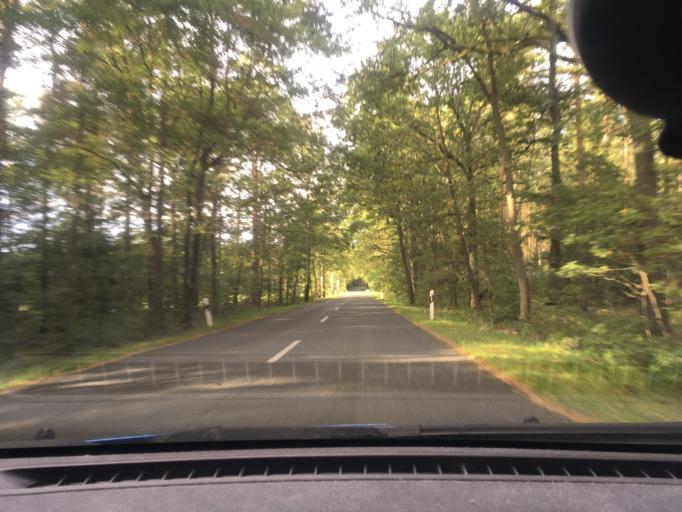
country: DE
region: Lower Saxony
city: Gohrde
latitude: 53.1489
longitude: 10.8670
